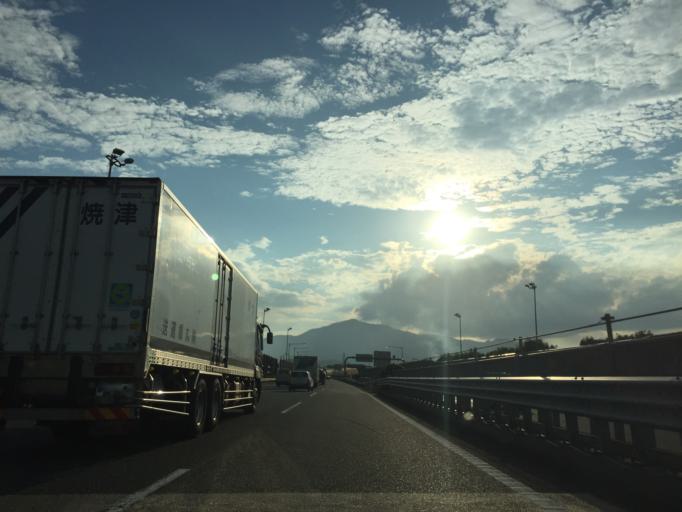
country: JP
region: Kanagawa
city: Atsugi
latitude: 35.4245
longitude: 139.3575
